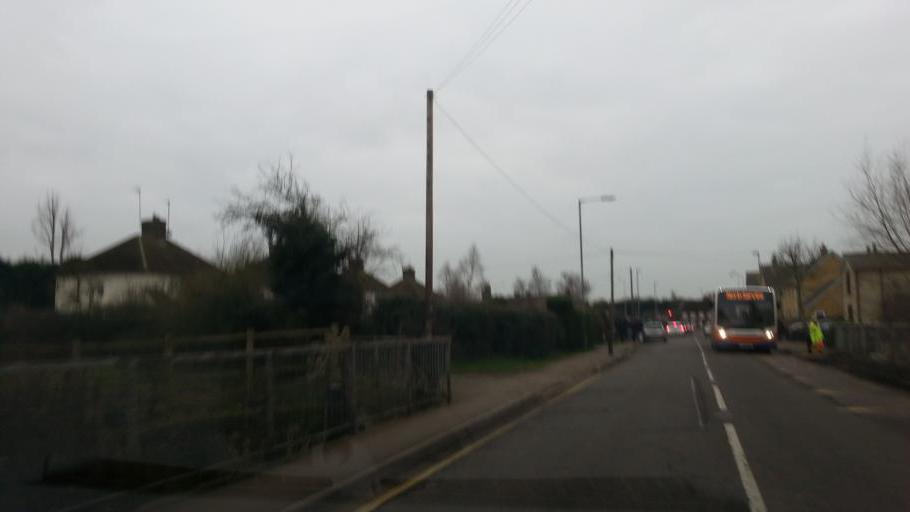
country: GB
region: England
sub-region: Central Bedfordshire
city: Hockliffe
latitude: 51.9326
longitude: -0.5858
